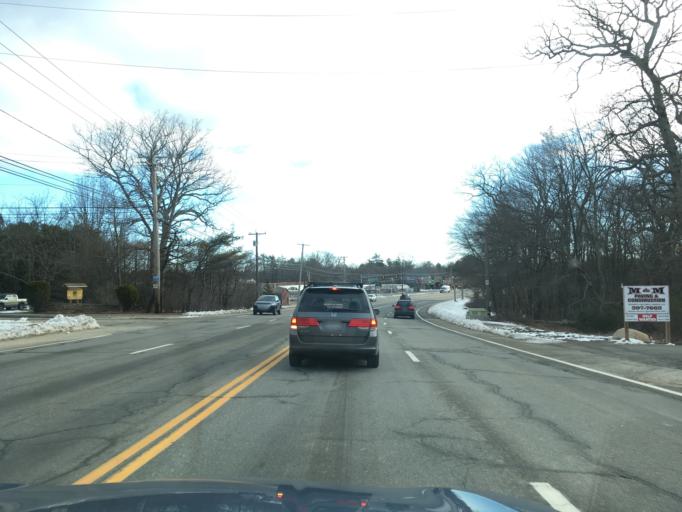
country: US
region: Rhode Island
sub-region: Kent County
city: West Warwick
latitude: 41.6777
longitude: -71.5887
